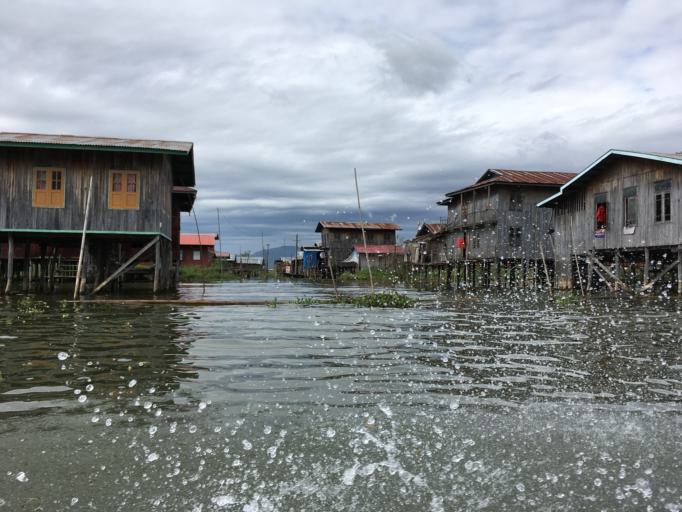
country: MM
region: Shan
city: Taunggyi
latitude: 20.4543
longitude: 96.9070
